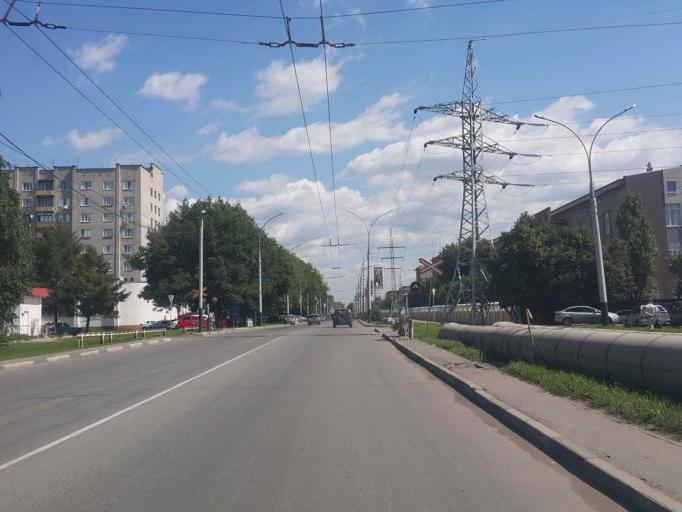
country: RU
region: Tambov
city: Tambov
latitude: 52.7486
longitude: 41.4598
